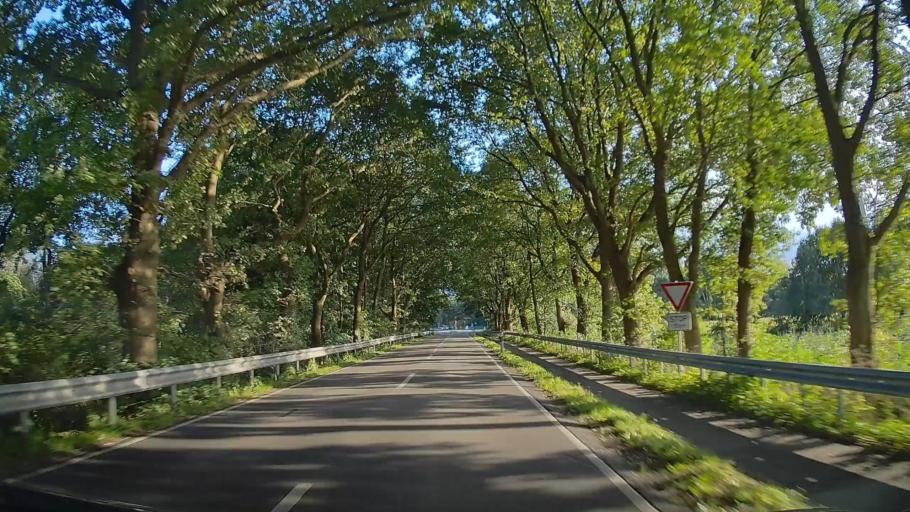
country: DE
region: Lower Saxony
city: Hilkenbrook
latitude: 53.0285
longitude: 7.7467
